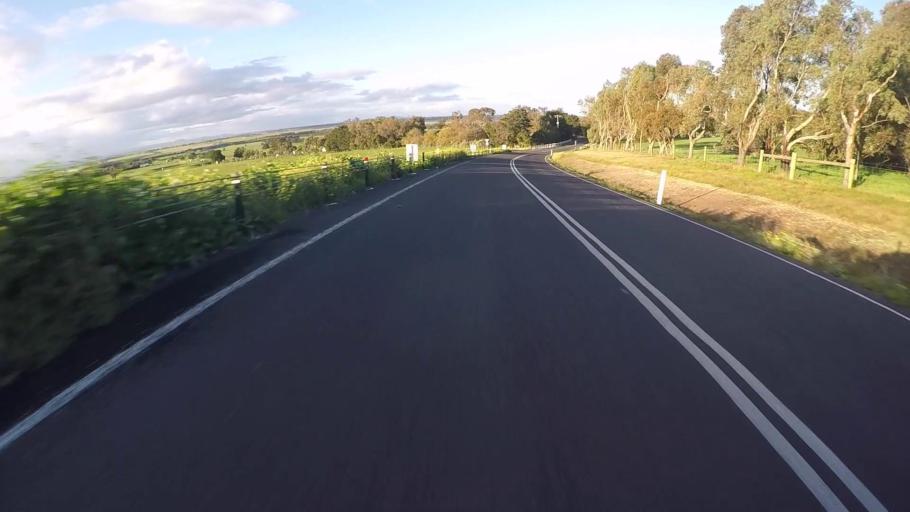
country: AU
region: Victoria
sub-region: Greater Geelong
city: Wandana Heights
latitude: -38.1551
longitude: 144.1644
